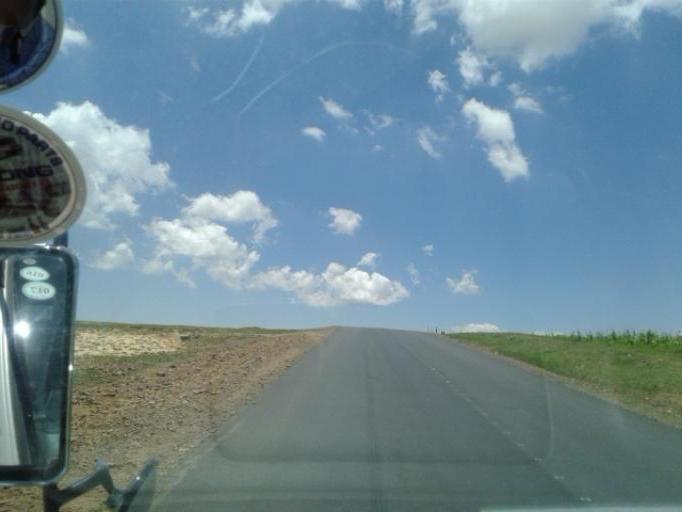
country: LS
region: Maseru
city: Maseru
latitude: -29.3112
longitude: 27.5980
